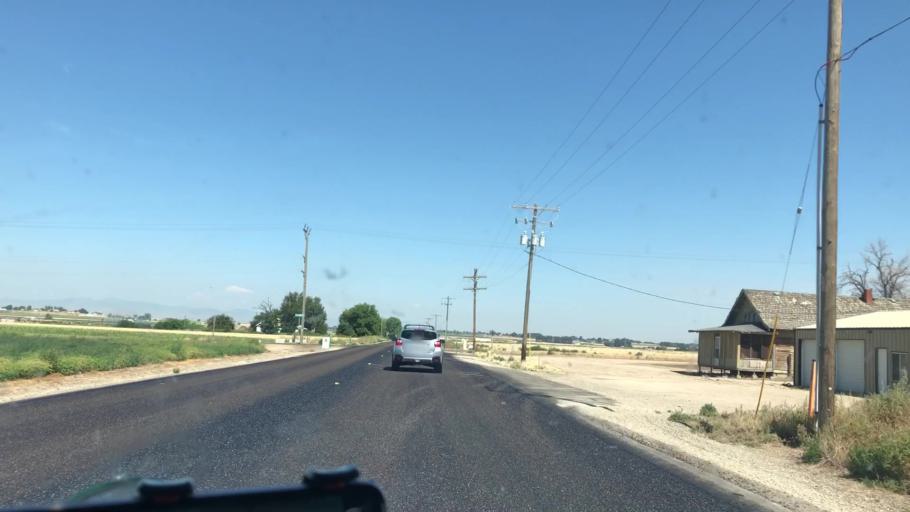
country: US
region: Idaho
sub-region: Owyhee County
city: Marsing
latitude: 43.6031
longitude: -116.7738
